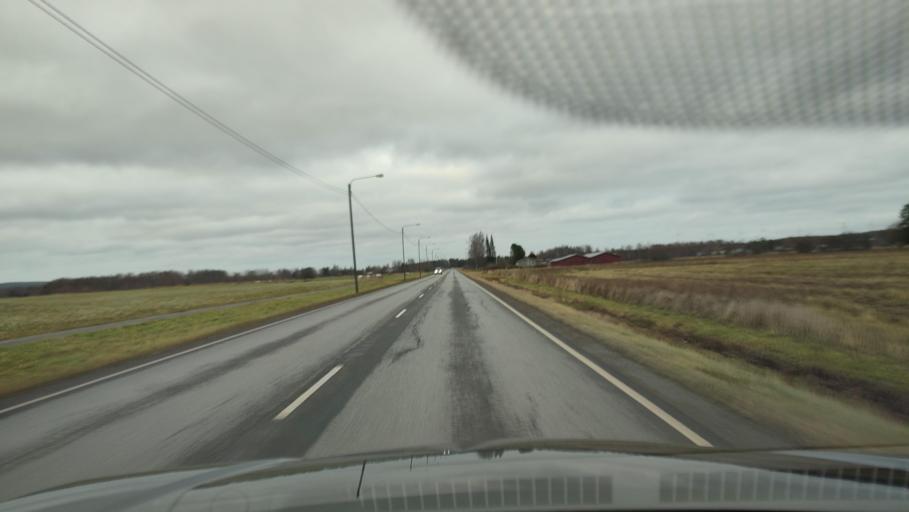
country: FI
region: Southern Ostrobothnia
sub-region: Seinaejoki
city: Kurikka
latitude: 62.6047
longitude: 22.4189
